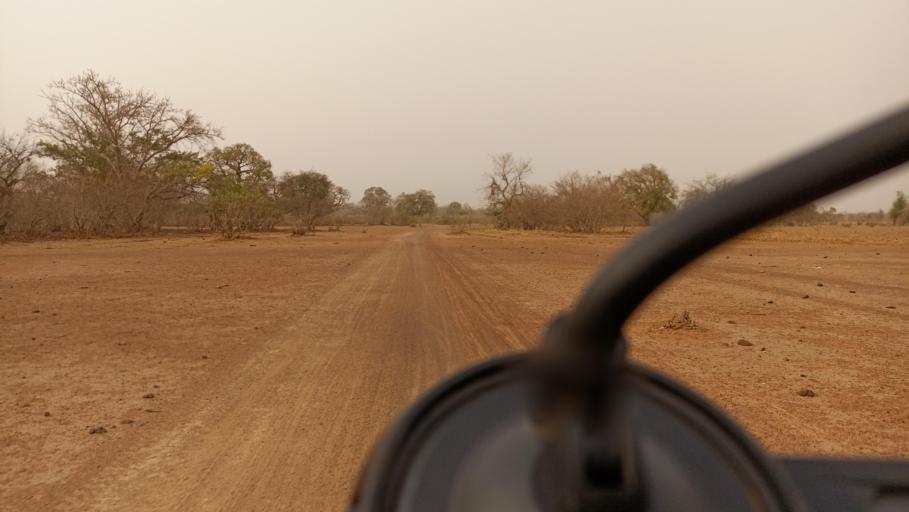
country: BF
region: Nord
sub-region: Province du Zondoma
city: Gourcy
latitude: 13.1710
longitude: -2.5883
